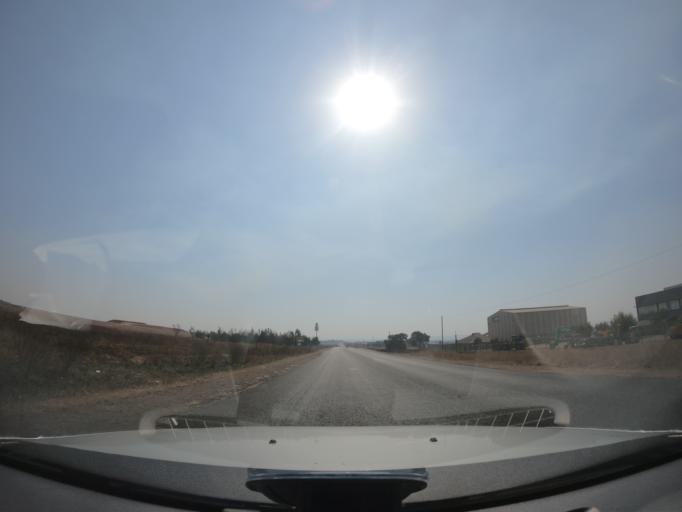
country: ZA
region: Mpumalanga
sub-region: Nkangala District Municipality
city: Middelburg
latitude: -25.8197
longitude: 29.4612
